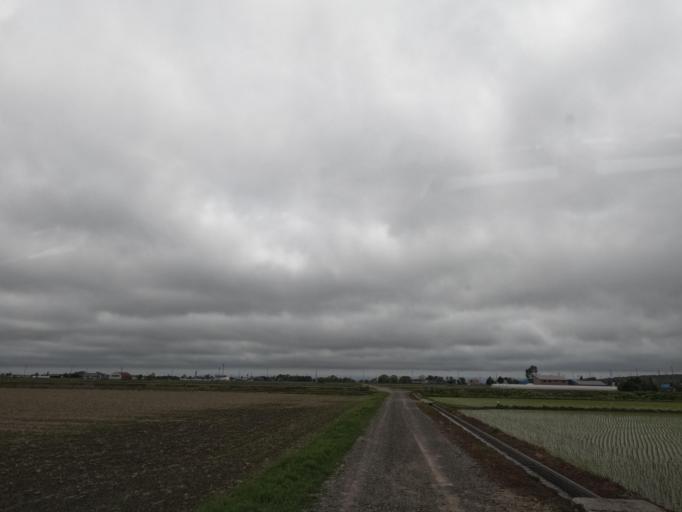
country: JP
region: Hokkaido
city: Tobetsu
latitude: 43.2468
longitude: 141.5197
